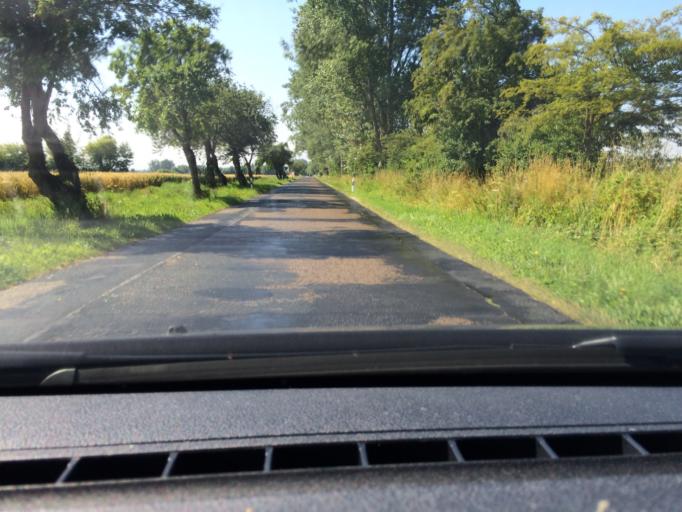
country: DE
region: Mecklenburg-Vorpommern
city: Niepars
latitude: 54.3548
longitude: 12.9032
